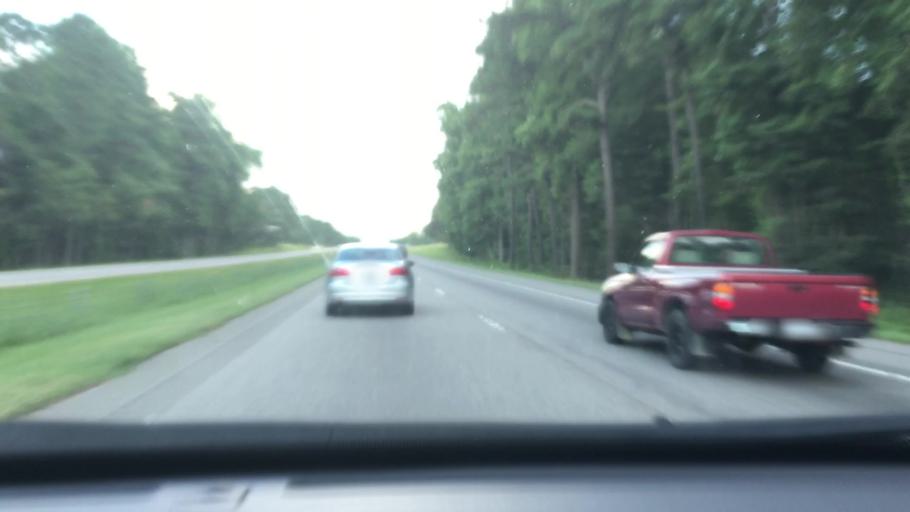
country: US
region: North Carolina
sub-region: Robeson County
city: Saint Pauls
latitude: 34.8606
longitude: -78.9653
